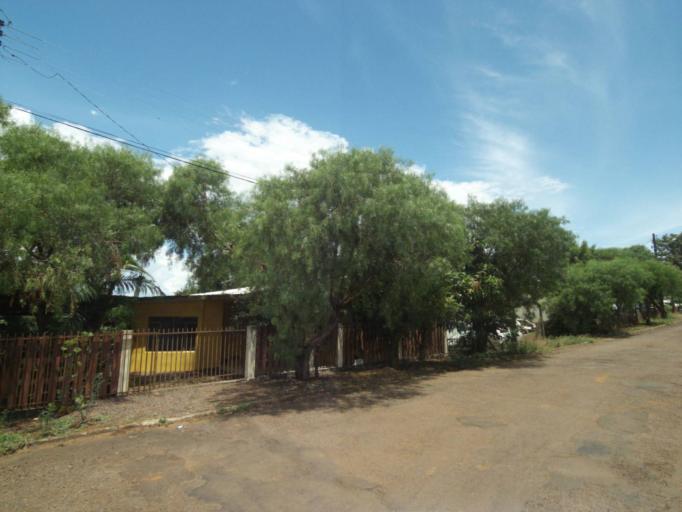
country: BR
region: Parana
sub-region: Guaraniacu
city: Guaraniacu
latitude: -25.1012
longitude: -52.8626
